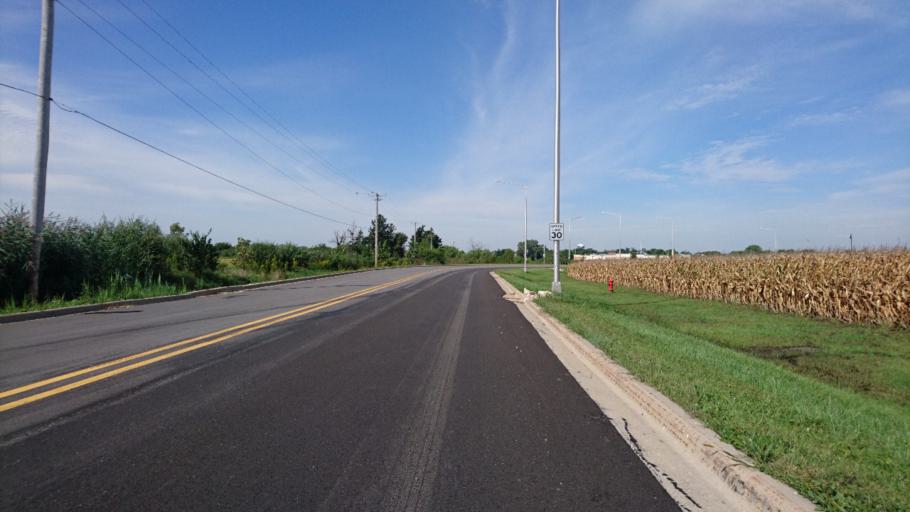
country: US
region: Illinois
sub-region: Will County
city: Elwood
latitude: 41.4044
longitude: -88.0990
